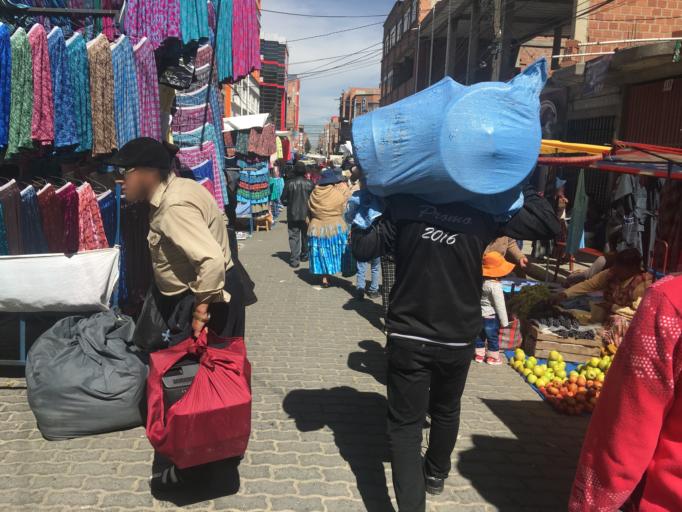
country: BO
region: La Paz
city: La Paz
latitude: -16.4911
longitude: -68.1717
